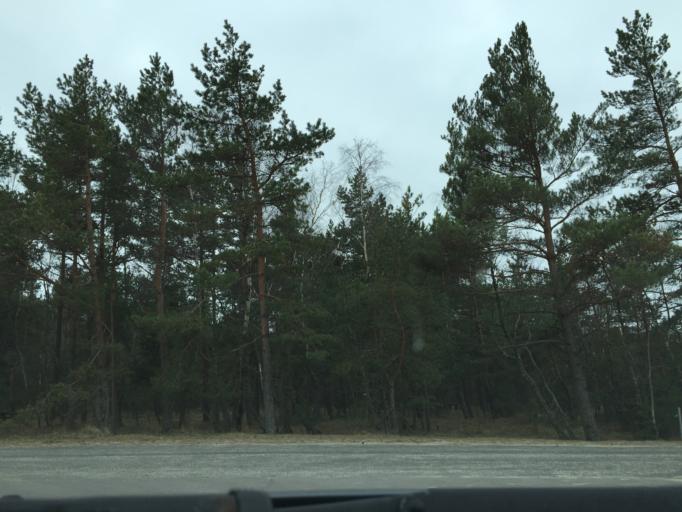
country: LT
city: Neringa
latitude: 55.4204
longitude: 21.0604
